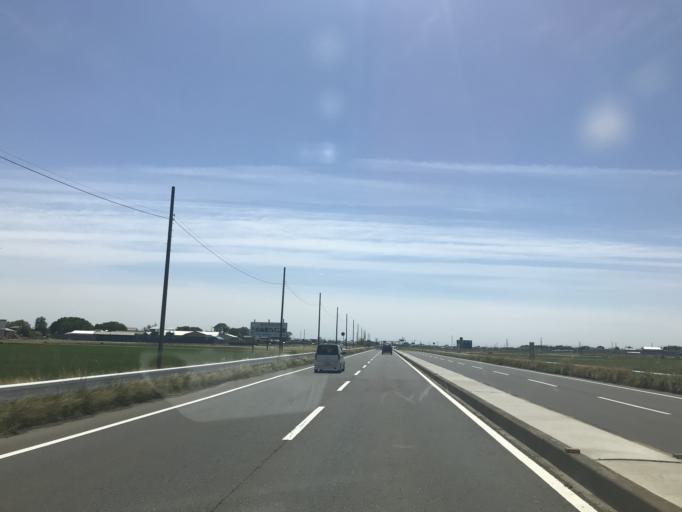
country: JP
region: Ibaraki
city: Shimodate
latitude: 36.2131
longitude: 139.9855
